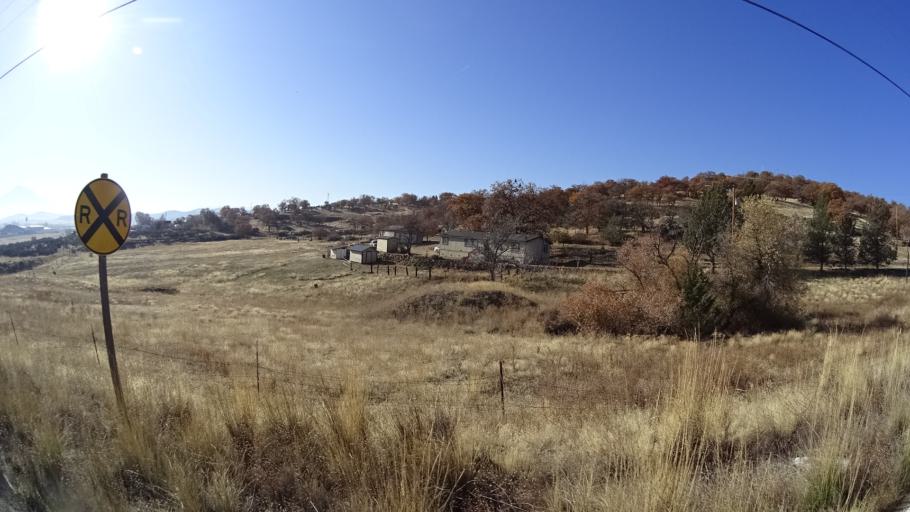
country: US
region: California
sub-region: Siskiyou County
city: Yreka
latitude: 41.7383
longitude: -122.6051
